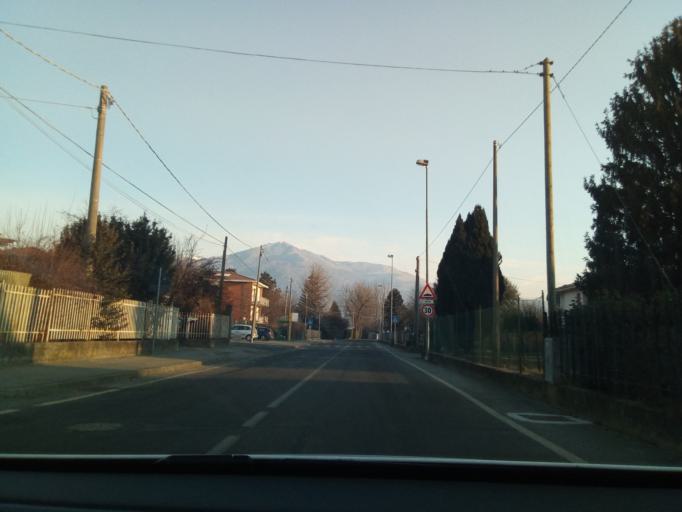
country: IT
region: Piedmont
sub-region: Provincia di Torino
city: Fiorano Canavese
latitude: 45.4692
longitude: 7.8326
